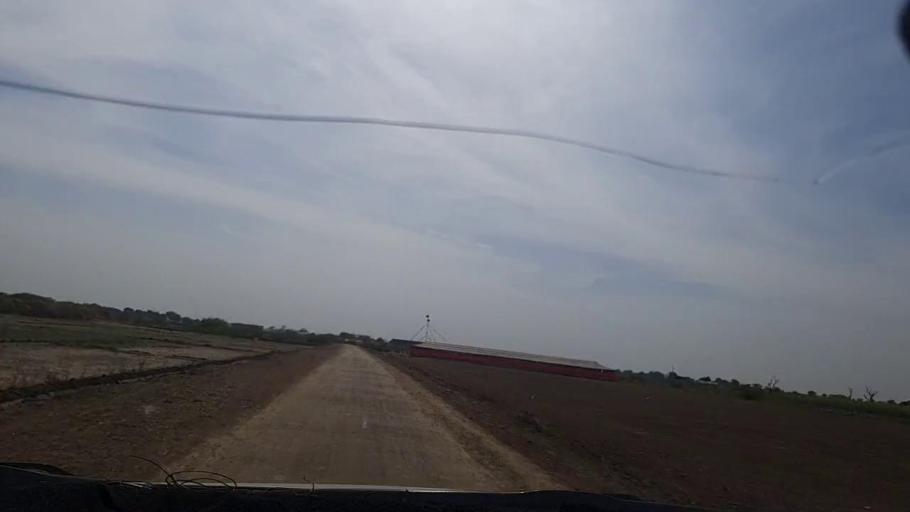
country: PK
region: Sindh
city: Dhoro Naro
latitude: 25.4379
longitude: 69.4974
